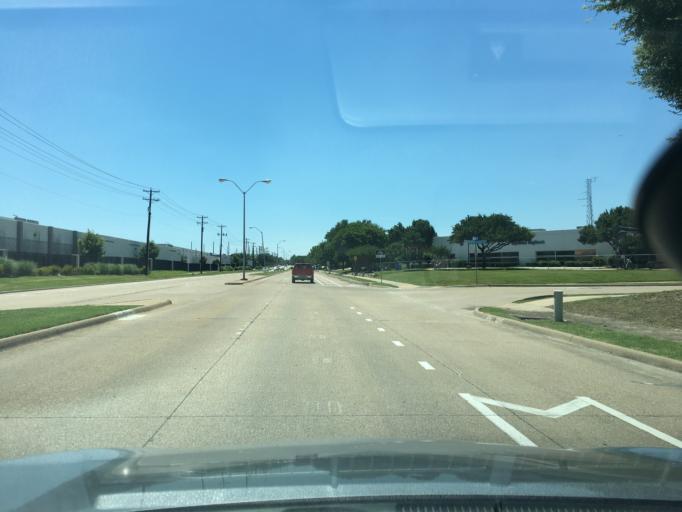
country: US
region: Texas
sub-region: Dallas County
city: Richardson
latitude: 32.9681
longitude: -96.7096
